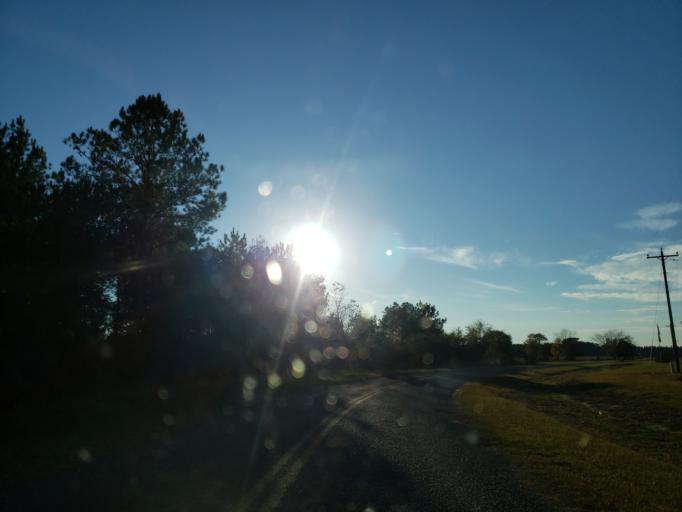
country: US
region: Georgia
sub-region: Dooly County
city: Unadilla
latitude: 32.2079
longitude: -83.7906
